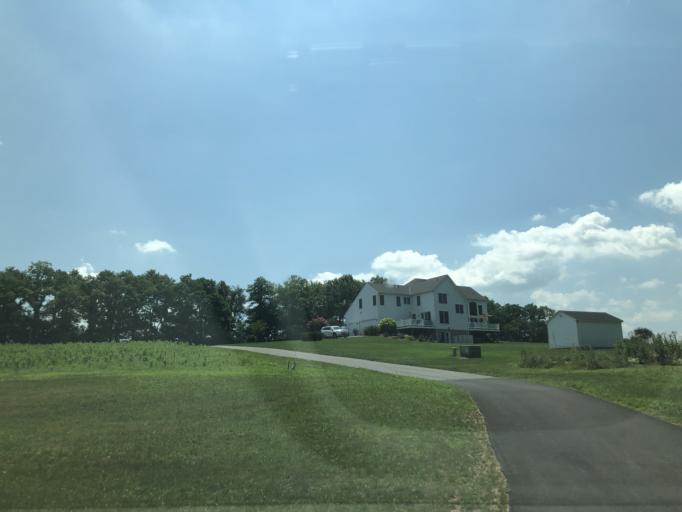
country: US
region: Maryland
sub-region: Carroll County
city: Westminster
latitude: 39.5243
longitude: -76.9482
